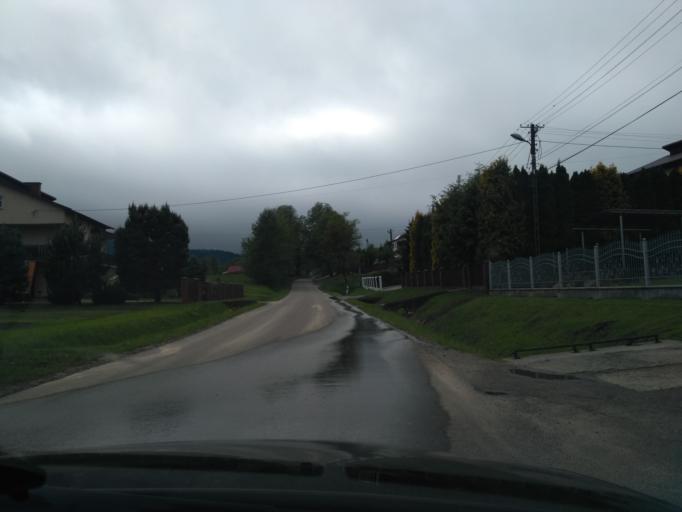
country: PL
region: Subcarpathian Voivodeship
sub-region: Powiat jasielski
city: Brzyska
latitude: 49.8234
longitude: 21.3860
